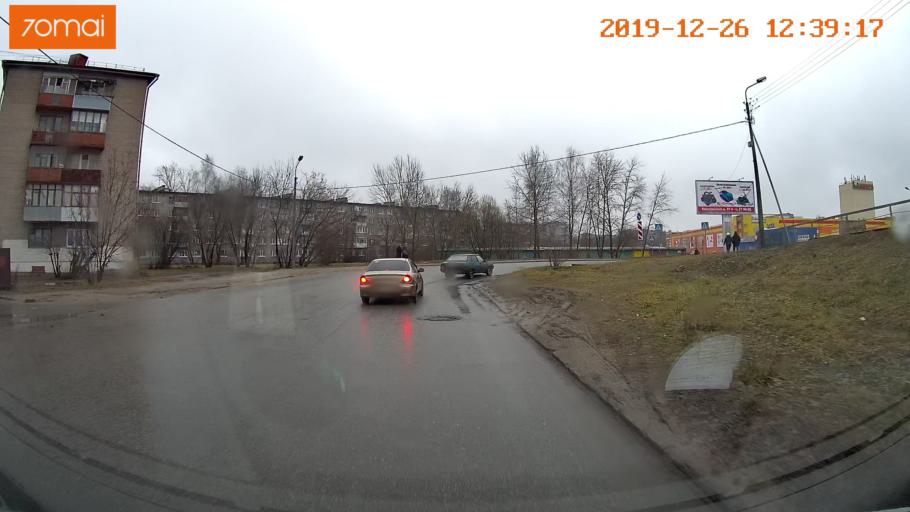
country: RU
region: Vologda
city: Tonshalovo
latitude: 59.1346
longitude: 37.9787
